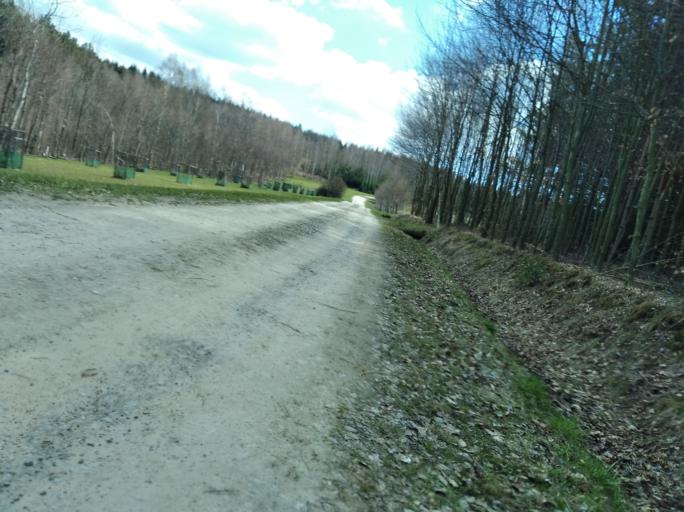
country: PL
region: Subcarpathian Voivodeship
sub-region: Powiat strzyzowski
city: Wysoka Strzyzowska
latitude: 49.8184
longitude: 21.7813
